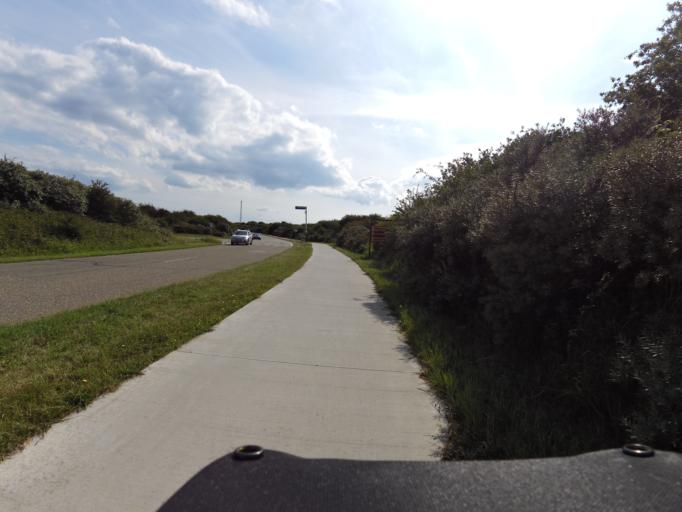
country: NL
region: Zeeland
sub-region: Schouwen-Duiveland
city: Scharendijke
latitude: 51.7891
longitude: 3.8715
